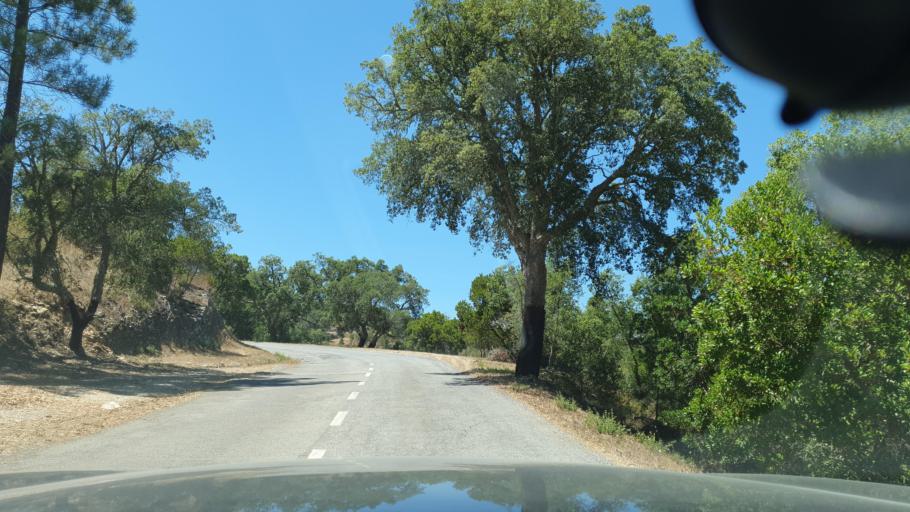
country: PT
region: Beja
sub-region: Odemira
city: Odemira
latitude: 37.6074
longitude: -8.4967
